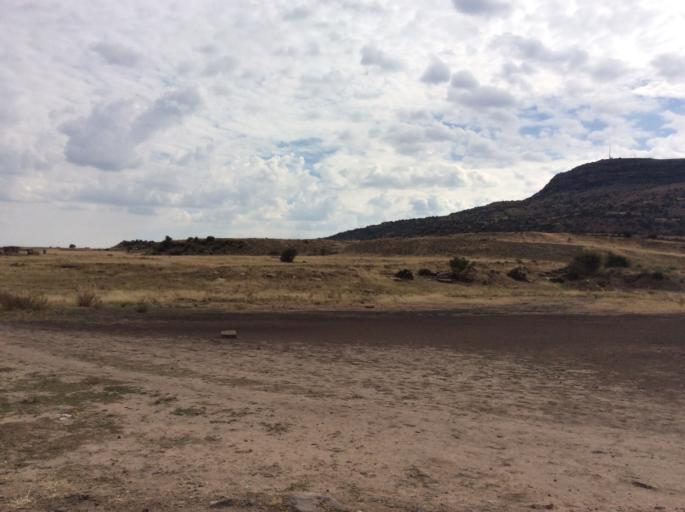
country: LS
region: Mafeteng
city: Mafeteng
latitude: -29.7183
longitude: 27.0245
